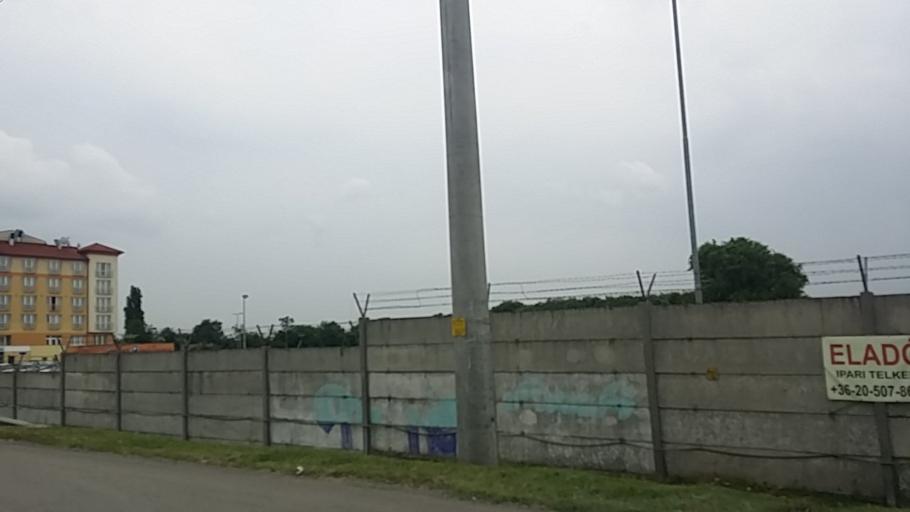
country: HU
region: Pest
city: Gyal
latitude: 47.4155
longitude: 19.2430
